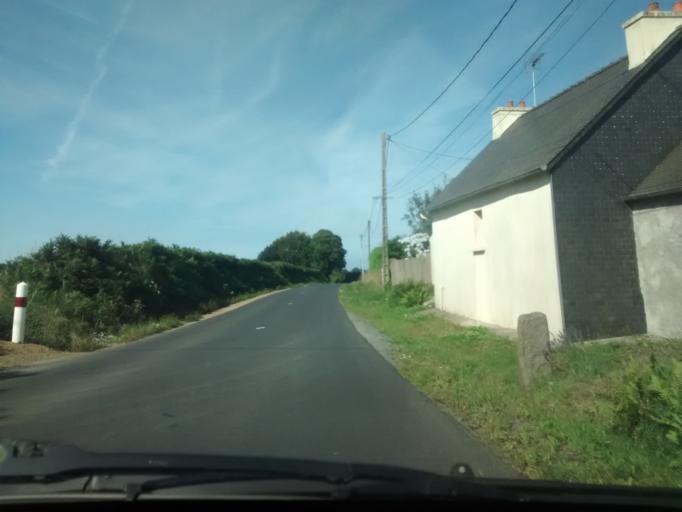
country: FR
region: Brittany
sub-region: Departement des Cotes-d'Armor
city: Rospez
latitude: 48.7593
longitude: -3.3961
